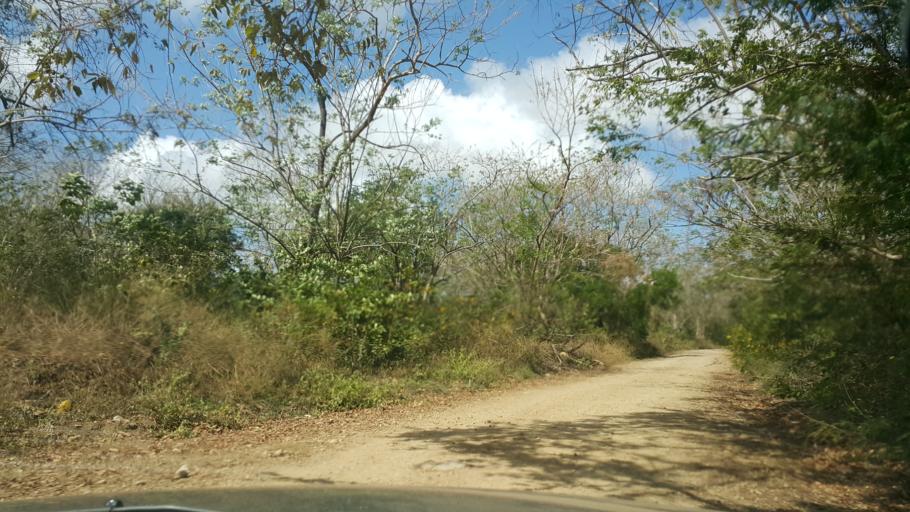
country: NI
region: Rivas
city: San Juan del Sur
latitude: 11.3090
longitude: -85.8413
